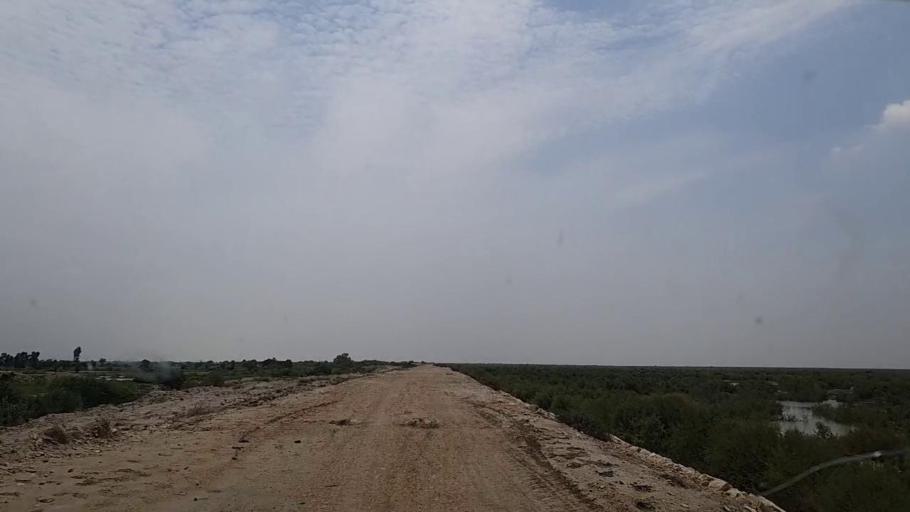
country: PK
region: Sindh
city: Phulji
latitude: 26.8621
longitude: 67.6384
